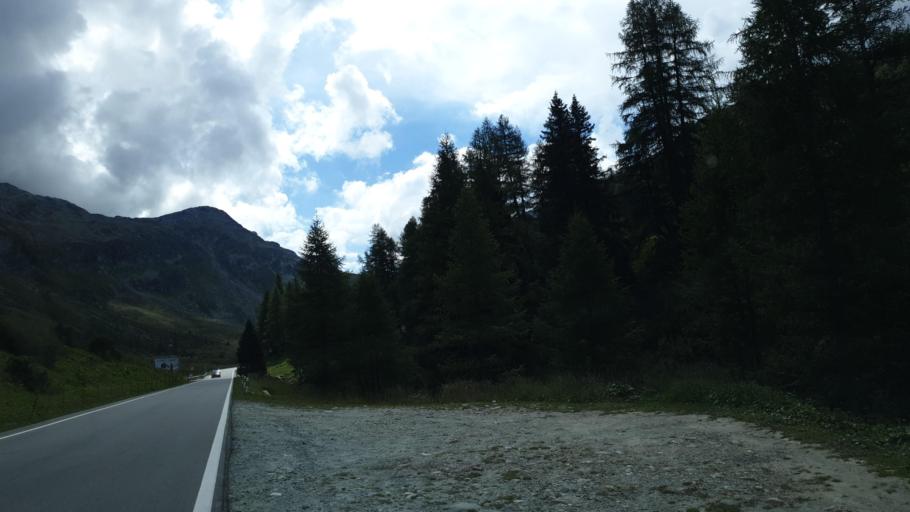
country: IT
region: Lombardy
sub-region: Provincia di Sondrio
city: Campodolcino
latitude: 46.5268
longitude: 9.3293
